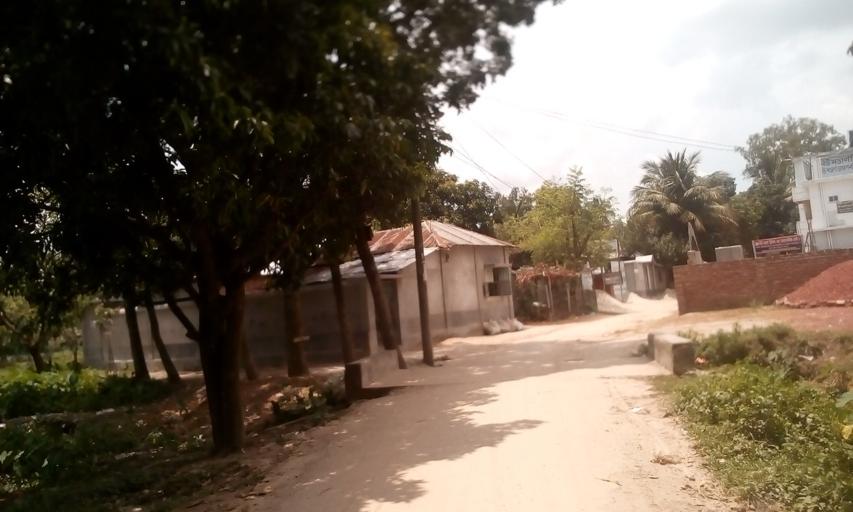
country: IN
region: West Bengal
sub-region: Dakshin Dinajpur
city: Balurghat
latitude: 25.3932
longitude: 88.9877
